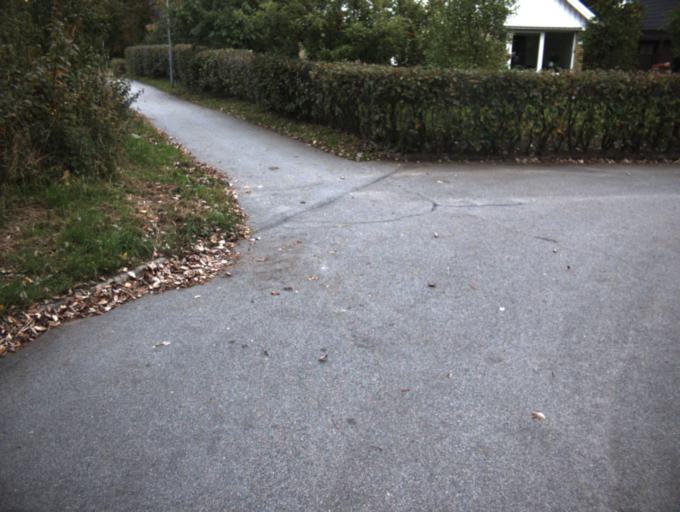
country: SE
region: Skane
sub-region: Helsingborg
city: Odakra
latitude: 56.1076
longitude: 12.7552
